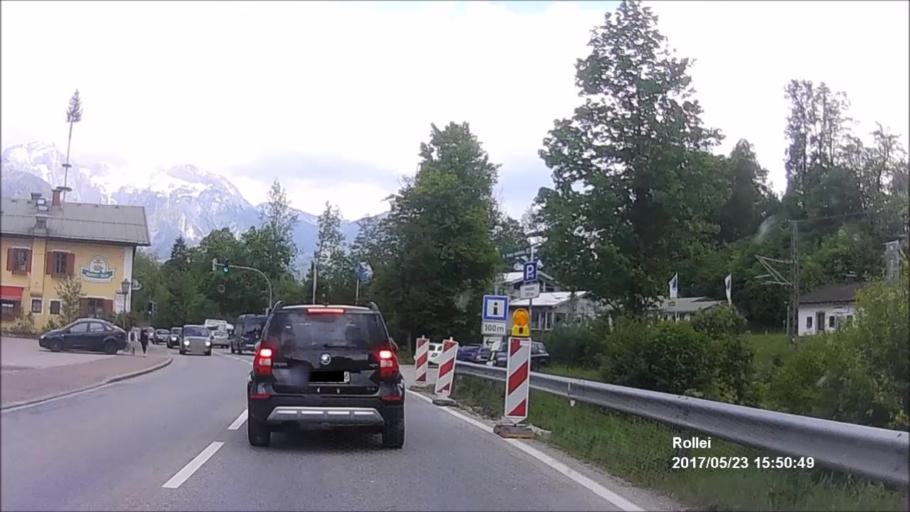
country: DE
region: Bavaria
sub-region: Upper Bavaria
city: Bischofswiesen
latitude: 47.6505
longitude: 12.9619
